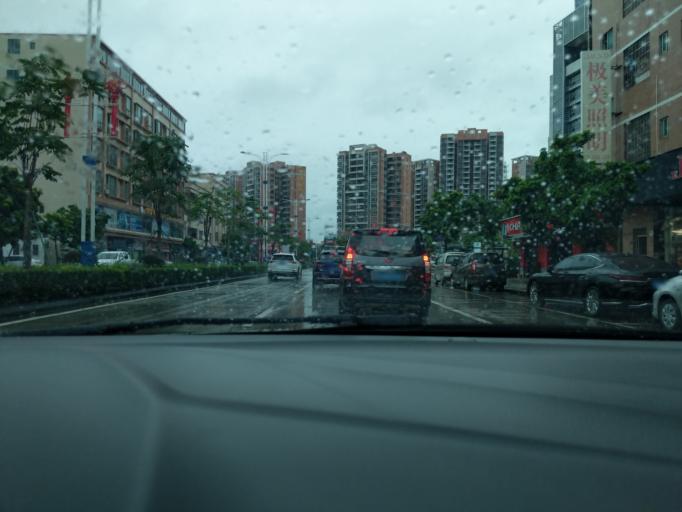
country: CN
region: Guangdong
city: Pingshi
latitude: 22.2011
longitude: 112.3299
